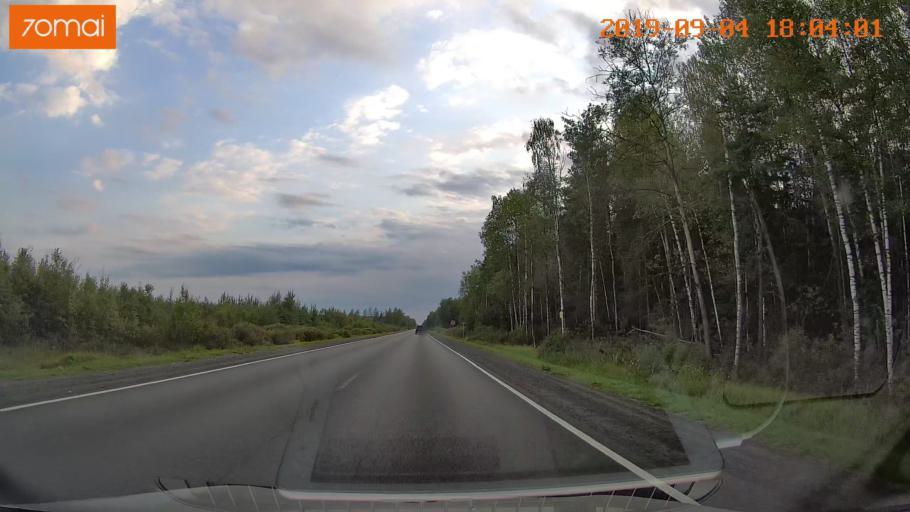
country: RU
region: Moskovskaya
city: Il'inskiy Pogost
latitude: 55.4571
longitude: 38.8448
